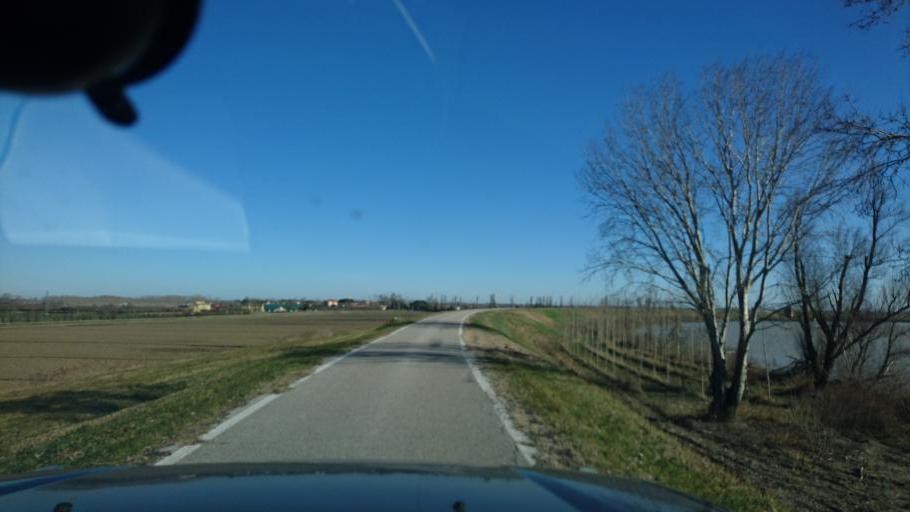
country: IT
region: Veneto
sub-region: Provincia di Rovigo
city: Papozze
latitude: 44.9427
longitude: 12.1680
